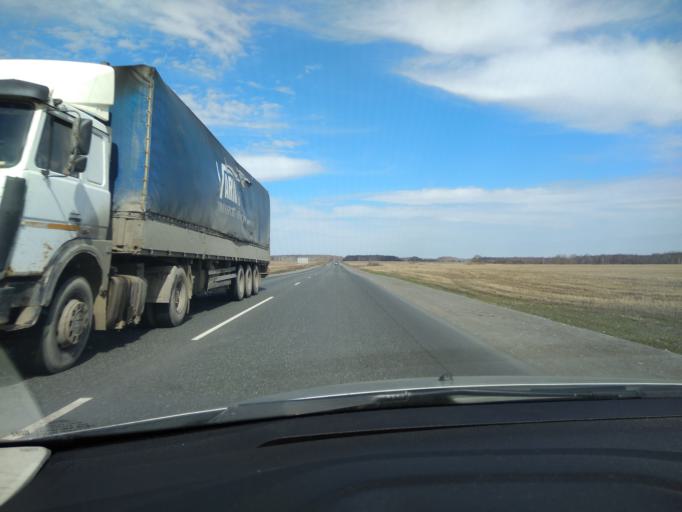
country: RU
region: Sverdlovsk
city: Pyshma
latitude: 56.9170
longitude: 63.1299
